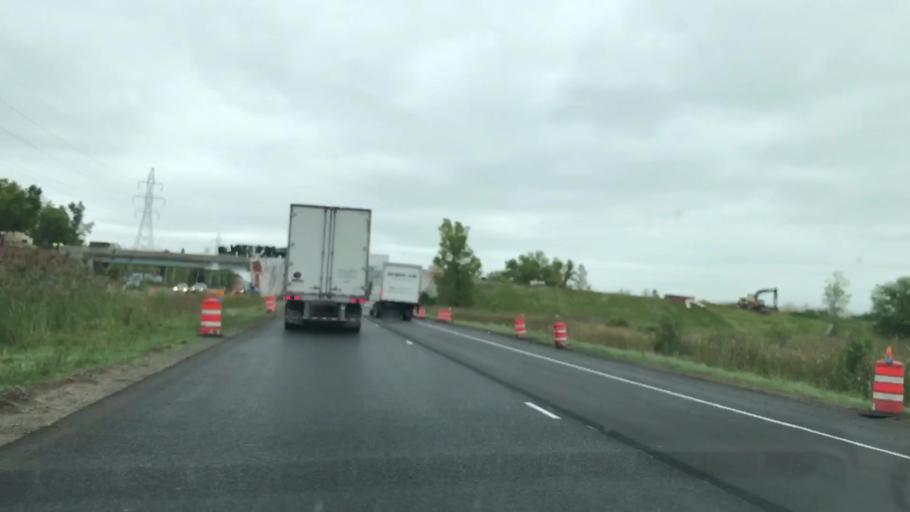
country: US
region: Wisconsin
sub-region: Brown County
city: Suamico
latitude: 44.6219
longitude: -88.0501
